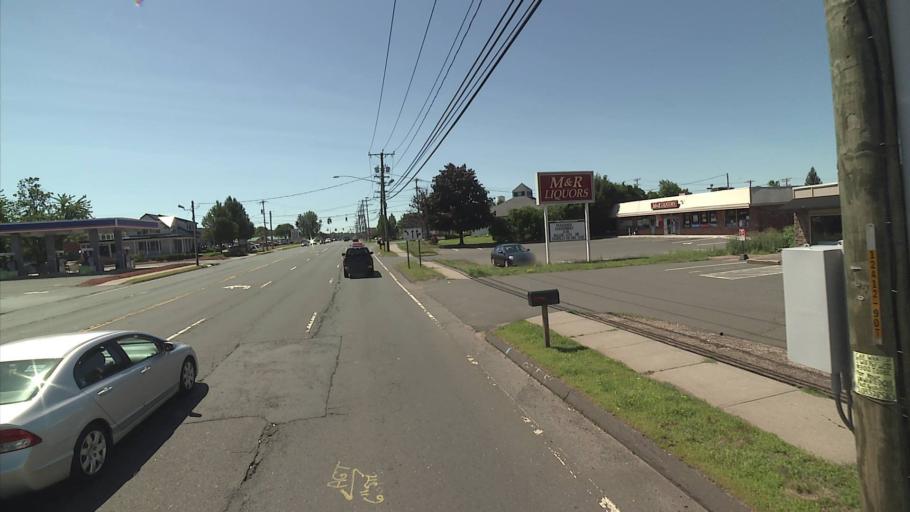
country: US
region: Connecticut
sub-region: Hartford County
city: Plainville
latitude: 41.6419
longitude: -72.8741
